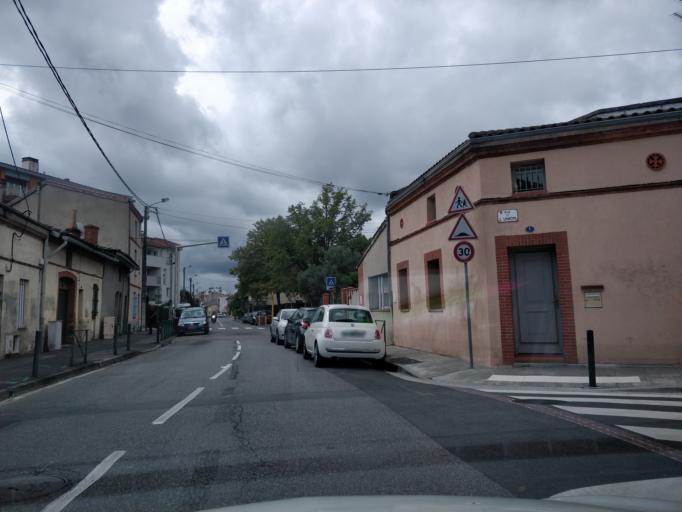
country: FR
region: Midi-Pyrenees
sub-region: Departement de la Haute-Garonne
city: Toulouse
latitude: 43.5893
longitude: 1.4198
